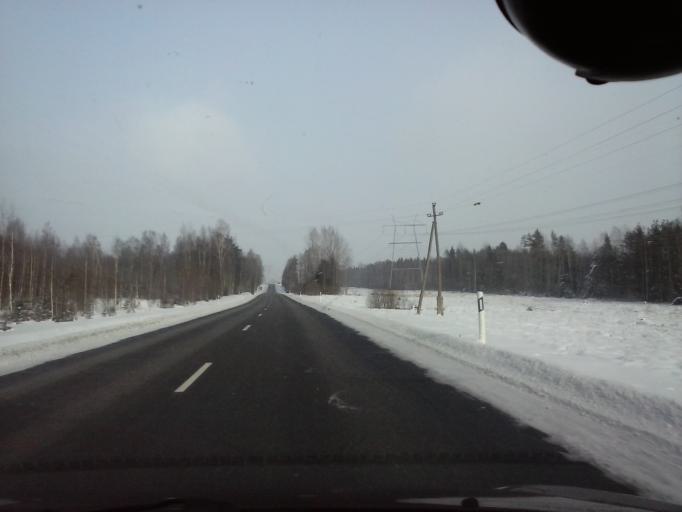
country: EE
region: Viljandimaa
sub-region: Abja vald
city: Abja-Paluoja
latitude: 58.2676
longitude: 25.2600
